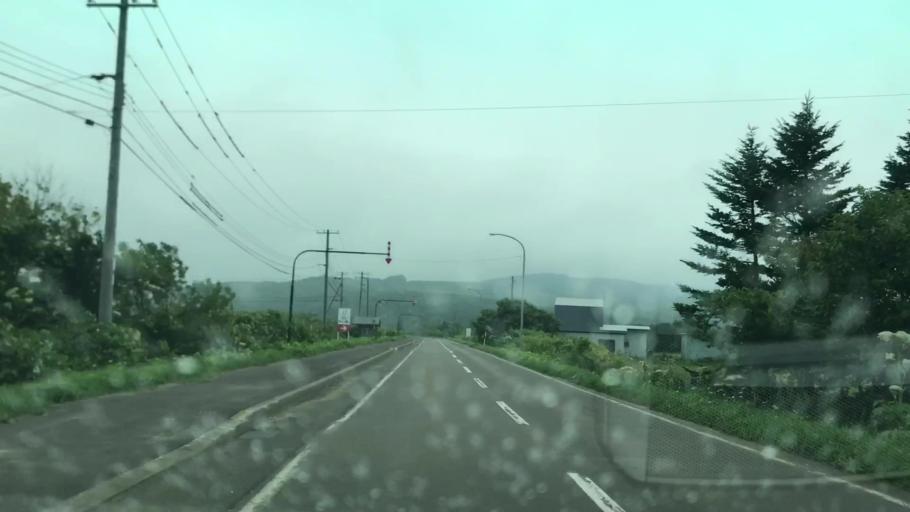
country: JP
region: Hokkaido
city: Iwanai
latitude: 42.7534
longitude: 140.2791
